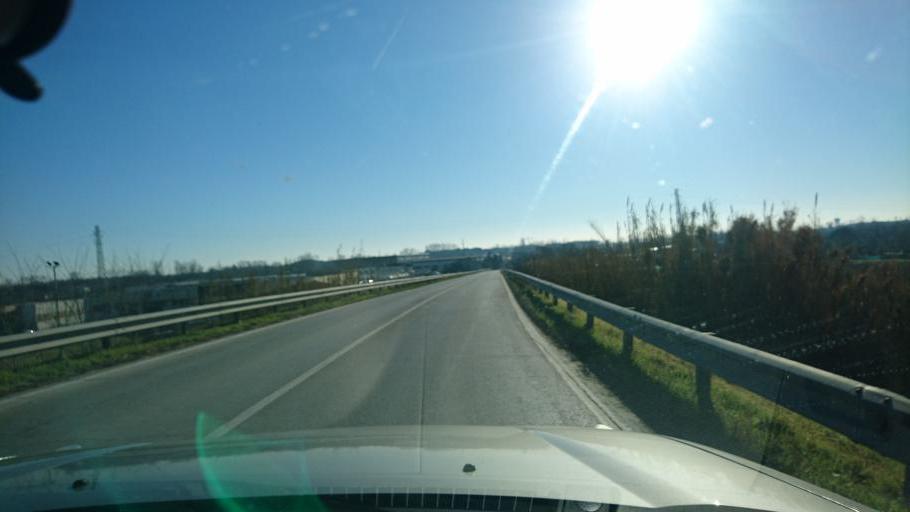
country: IT
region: Veneto
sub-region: Provincia di Rovigo
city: Porto Viro
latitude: 45.0473
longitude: 12.2101
